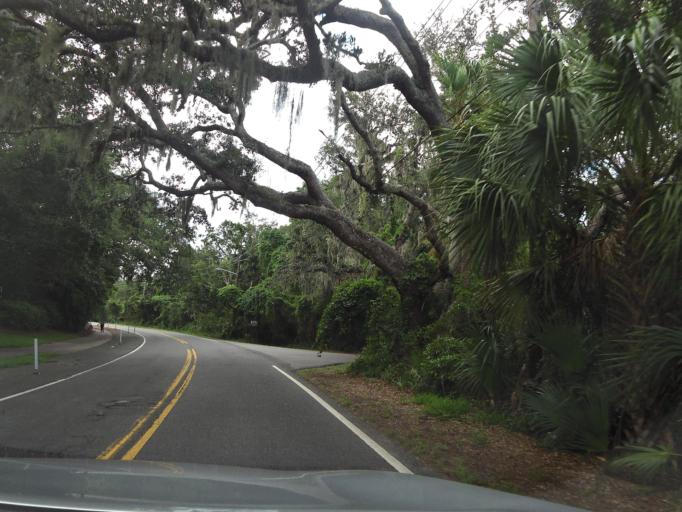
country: US
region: Georgia
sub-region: Glynn County
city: Saint Simons Island
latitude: 31.1560
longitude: -81.3804
